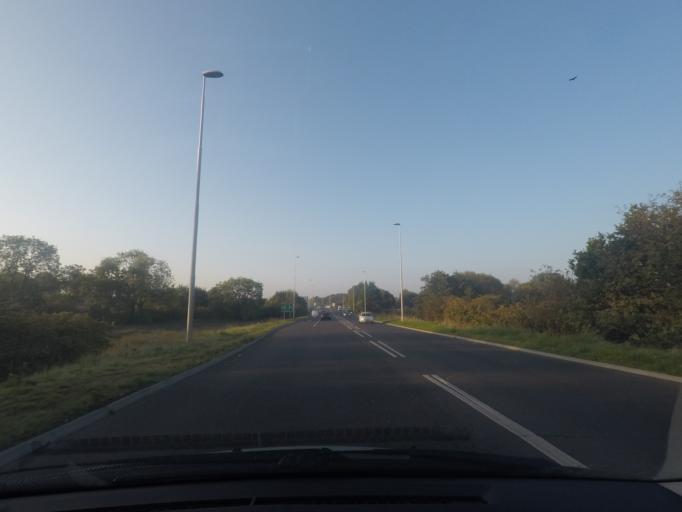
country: GB
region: England
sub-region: City of York
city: Nether Poppleton
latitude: 53.9750
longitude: -1.1410
